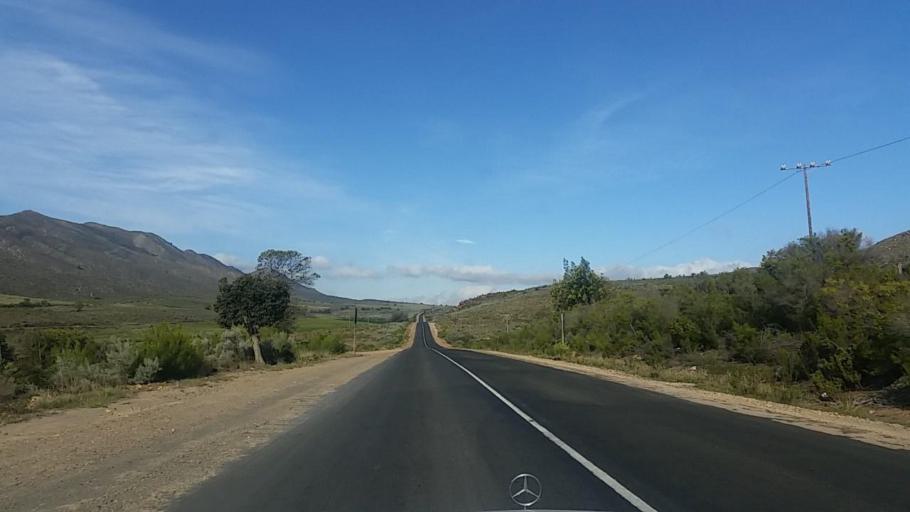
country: ZA
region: Western Cape
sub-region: Eden District Municipality
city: George
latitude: -33.8194
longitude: 22.3622
